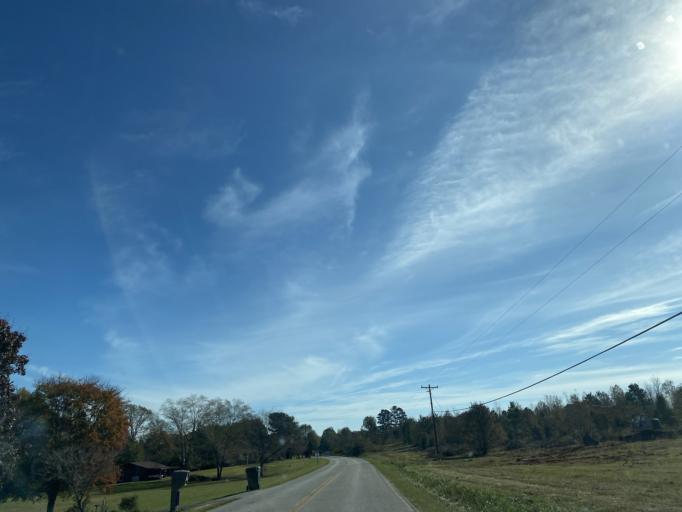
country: US
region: South Carolina
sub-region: Spartanburg County
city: Mayo
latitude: 35.0920
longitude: -81.8131
